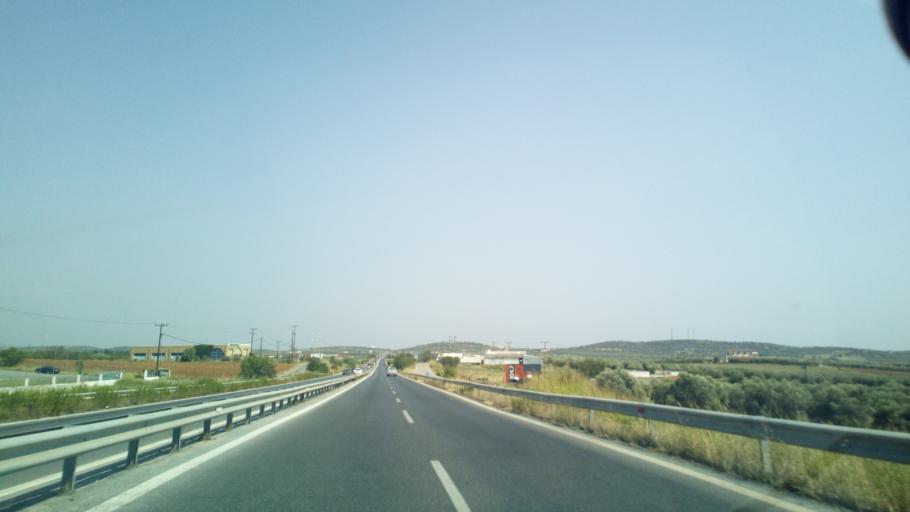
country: GR
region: Central Macedonia
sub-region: Nomos Chalkidikis
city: Nea Flogita
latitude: 40.2636
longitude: 23.2488
